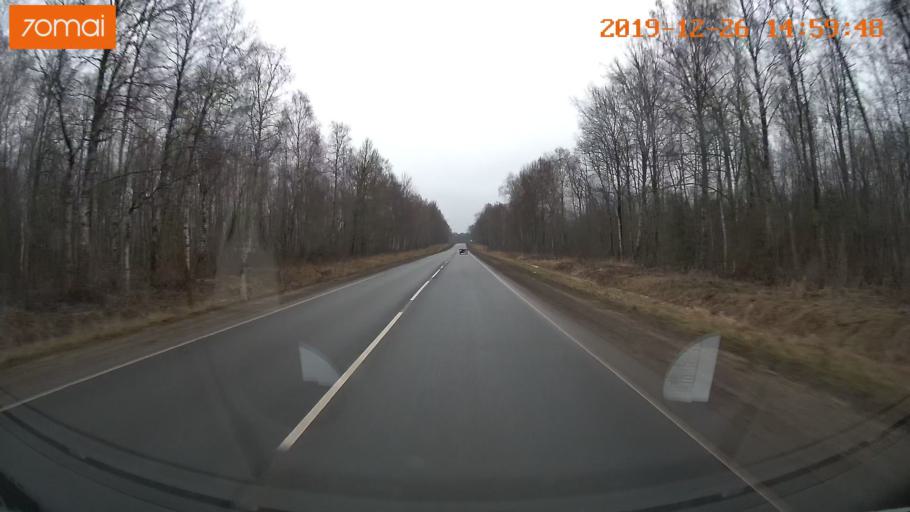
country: RU
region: Jaroslavl
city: Rybinsk
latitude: 58.2540
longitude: 38.8491
